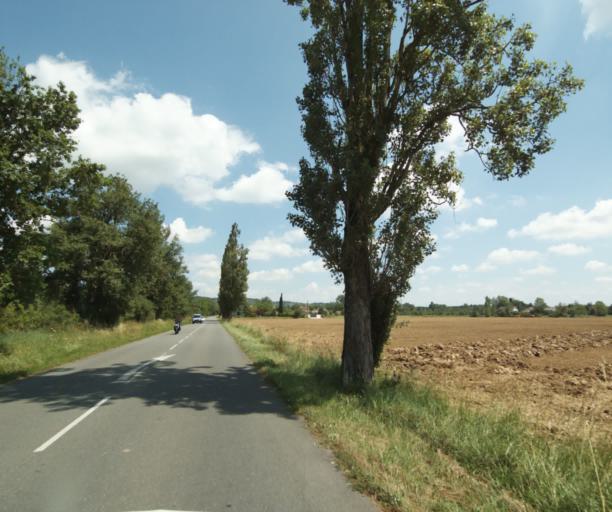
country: FR
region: Midi-Pyrenees
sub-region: Departement du Tarn-et-Garonne
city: Montauban
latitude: 44.0692
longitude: 1.3661
